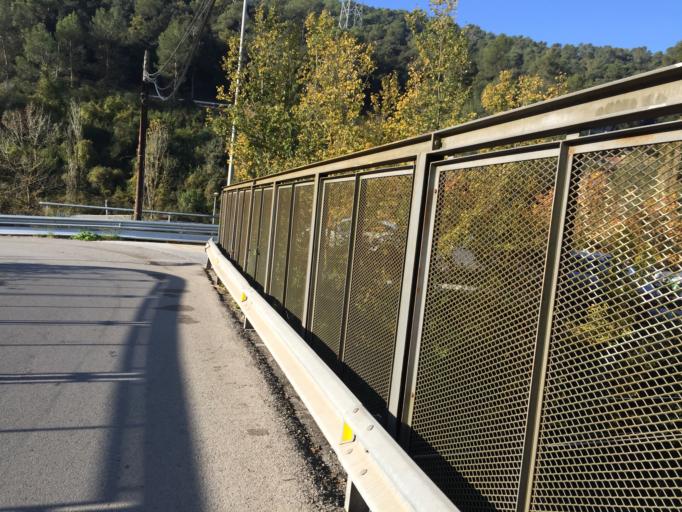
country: ES
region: Catalonia
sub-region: Provincia de Barcelona
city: Sant Just Desvern
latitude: 41.4207
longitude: 2.0964
